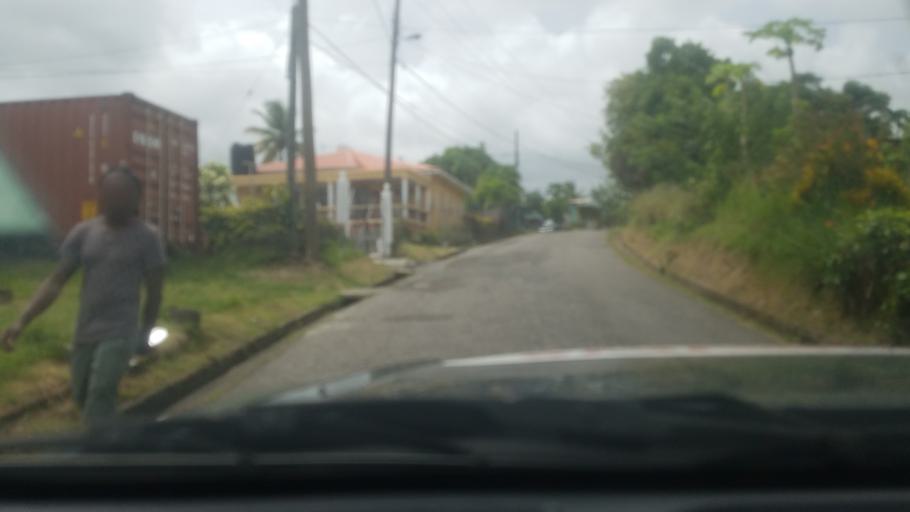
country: LC
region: Laborie Quarter
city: Laborie
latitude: 13.7579
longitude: -60.9806
